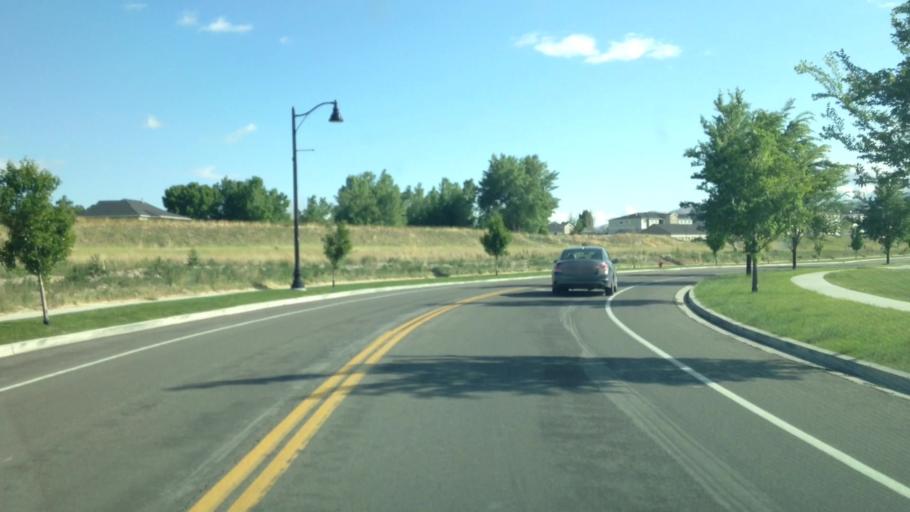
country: US
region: Utah
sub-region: Utah County
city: Saratoga Springs
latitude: 40.3928
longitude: -111.9238
